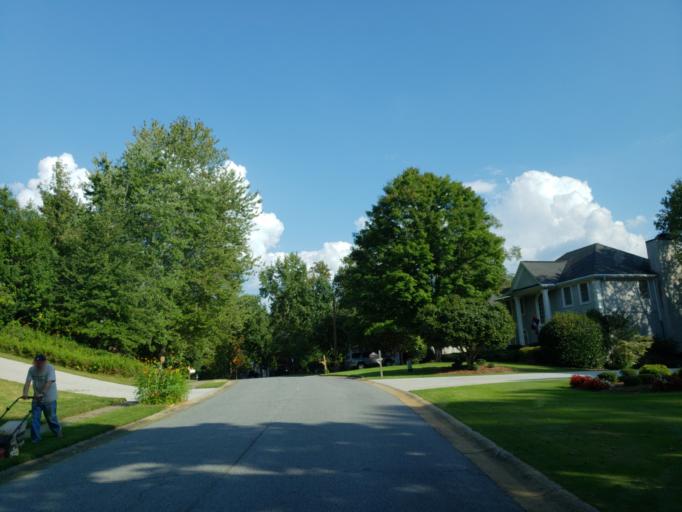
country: US
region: Georgia
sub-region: Cherokee County
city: Woodstock
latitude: 34.0592
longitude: -84.4474
